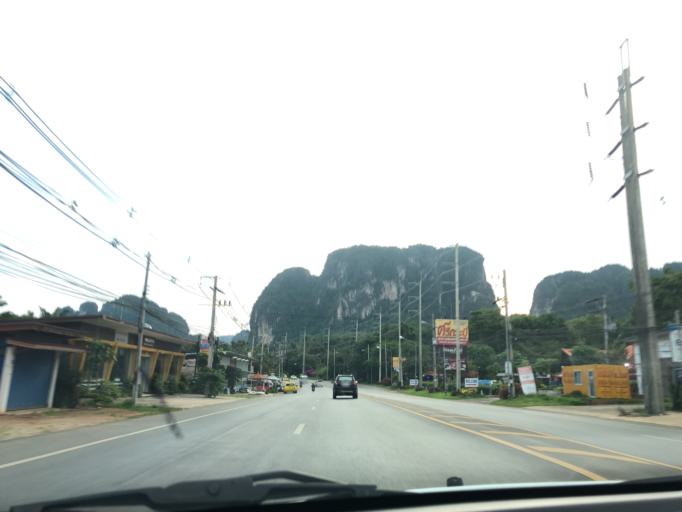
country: TH
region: Krabi
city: Krabi
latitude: 8.0826
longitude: 98.8625
